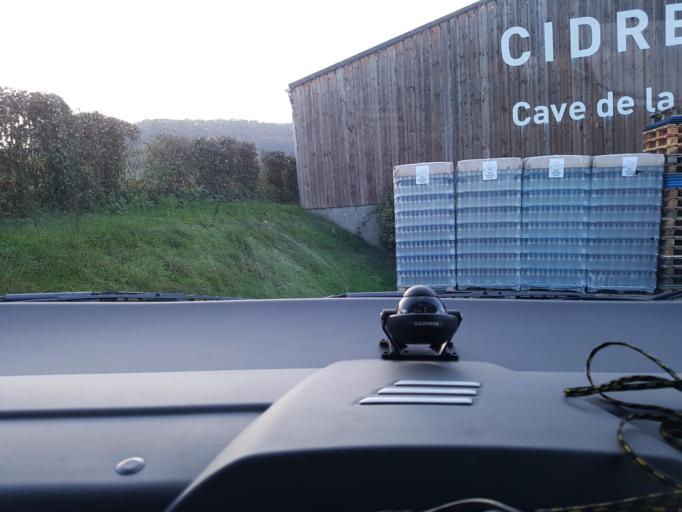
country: FR
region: Lower Normandy
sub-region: Departement du Calvados
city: Clecy
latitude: 48.8904
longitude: -0.4712
